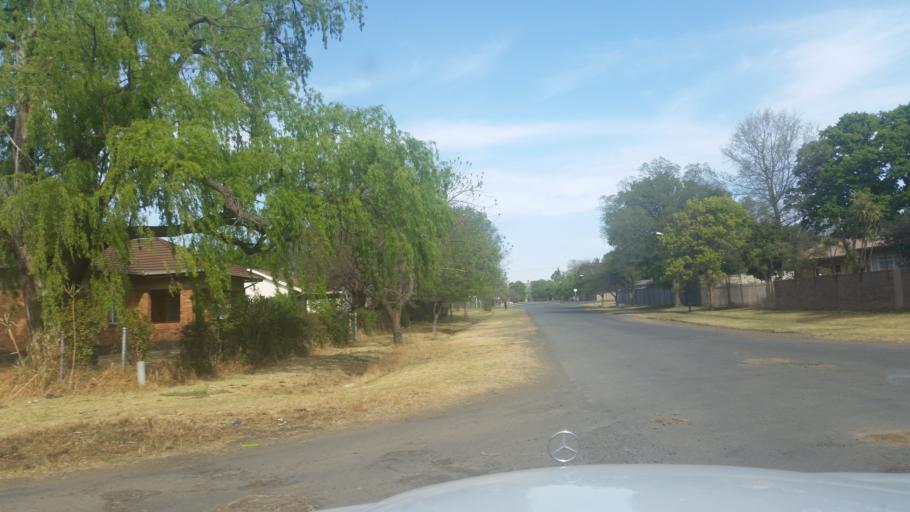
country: ZA
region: Orange Free State
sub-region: Thabo Mofutsanyana District Municipality
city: Harrismith
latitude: -28.2662
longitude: 29.1287
